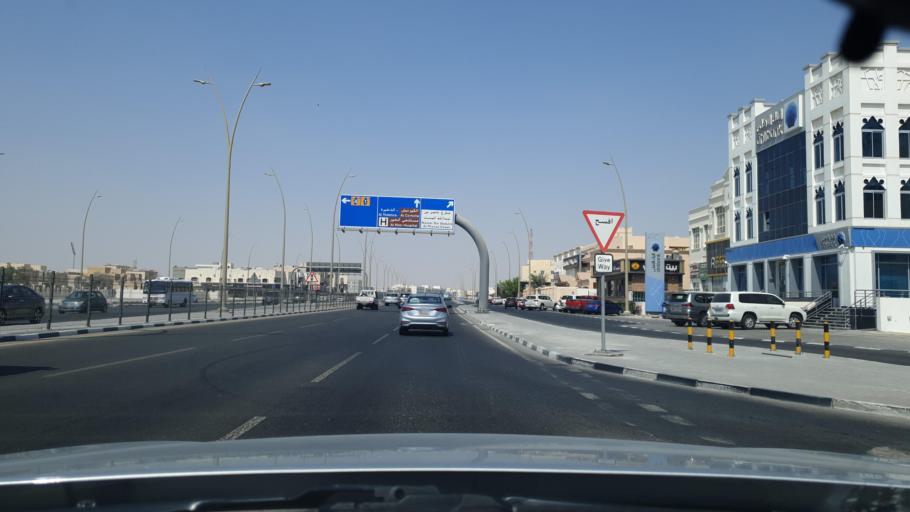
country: QA
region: Al Khawr
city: Al Khawr
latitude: 25.6767
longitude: 51.4998
